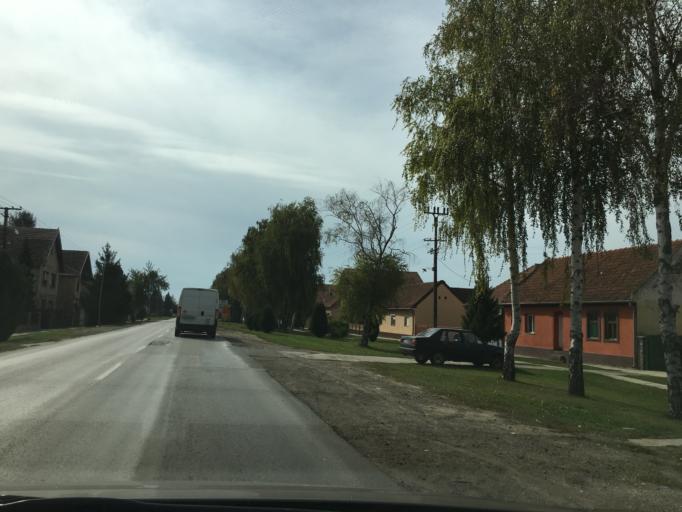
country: RS
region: Autonomna Pokrajina Vojvodina
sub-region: Juznobacki Okrug
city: Temerin
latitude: 45.3890
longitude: 19.8800
